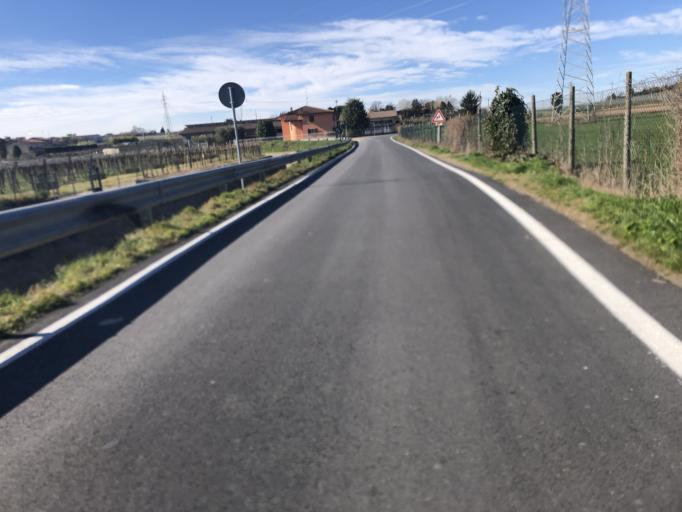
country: IT
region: Veneto
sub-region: Provincia di Verona
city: Sona
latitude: 45.4346
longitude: 10.8235
